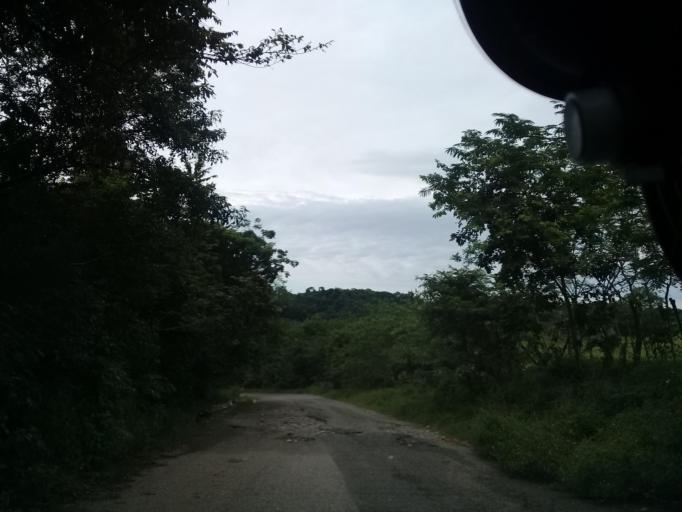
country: MX
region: Hidalgo
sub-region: Huejutla de Reyes
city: Chalahuiyapa
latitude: 21.2034
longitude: -98.3527
